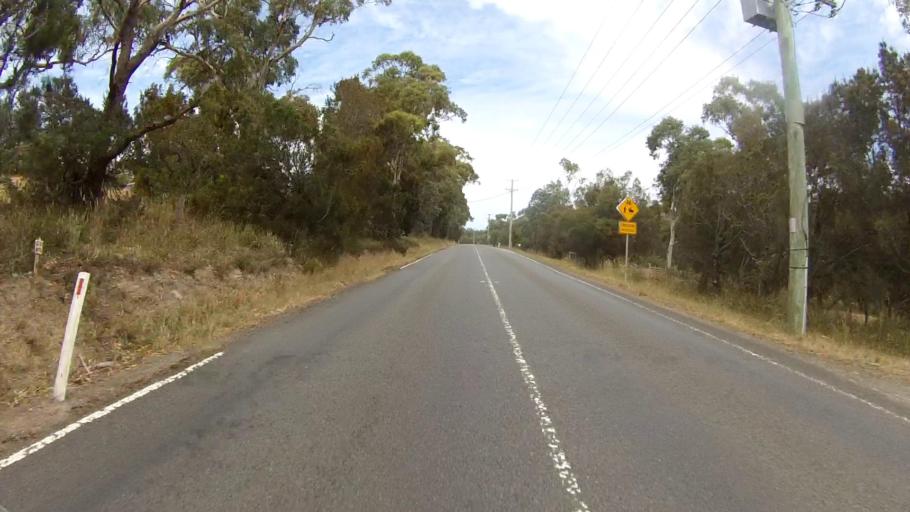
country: AU
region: Tasmania
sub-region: Clarence
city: Acton Park
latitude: -42.8710
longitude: 147.4834
